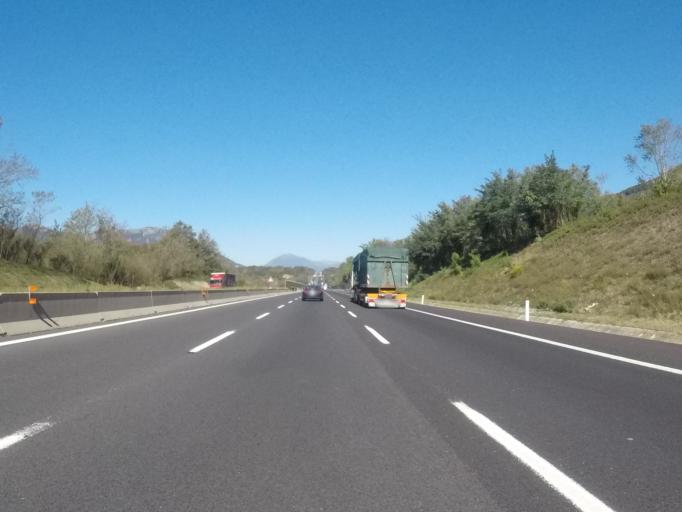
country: IT
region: Campania
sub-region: Provincia di Caserta
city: Tora
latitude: 41.3534
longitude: 14.0408
